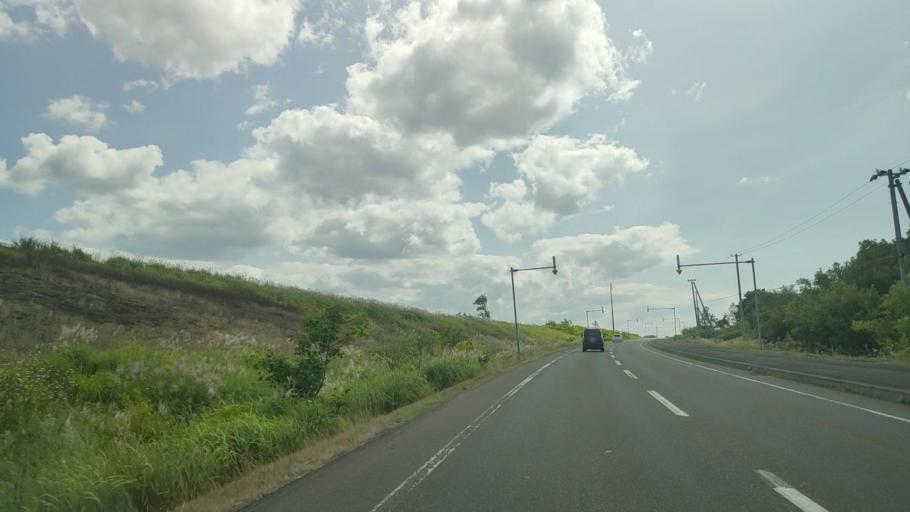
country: JP
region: Hokkaido
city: Makubetsu
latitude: 44.7912
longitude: 141.7903
